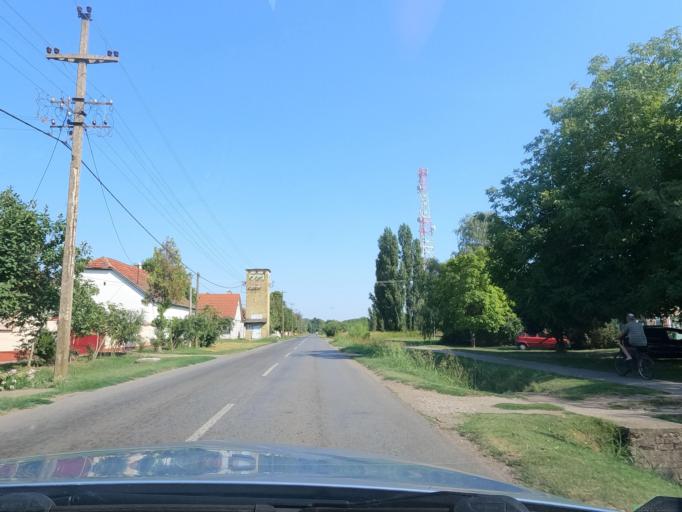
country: RS
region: Autonomna Pokrajina Vojvodina
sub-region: Juznobacki Okrug
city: Becej
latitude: 45.6250
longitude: 20.0292
